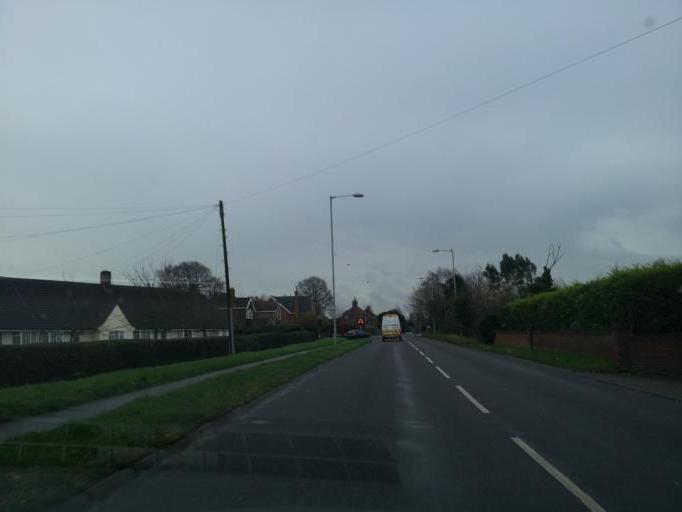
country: GB
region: England
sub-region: Norfolk
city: Brundall
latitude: 52.6334
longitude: 1.4412
